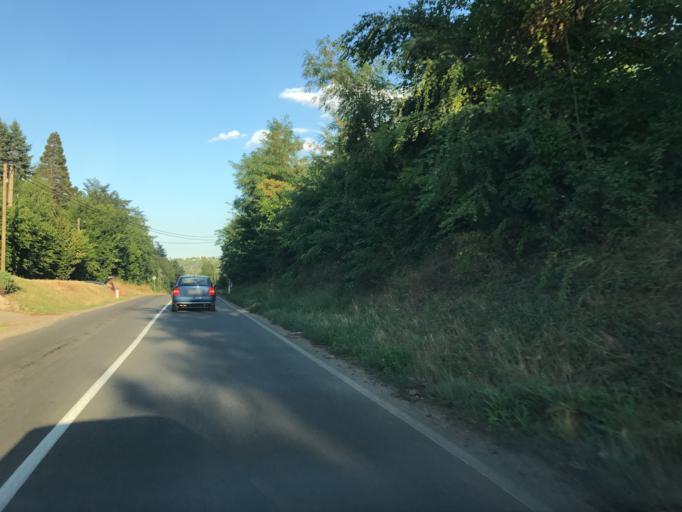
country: RS
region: Central Serbia
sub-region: Belgrade
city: Grocka
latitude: 44.6634
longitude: 20.7309
